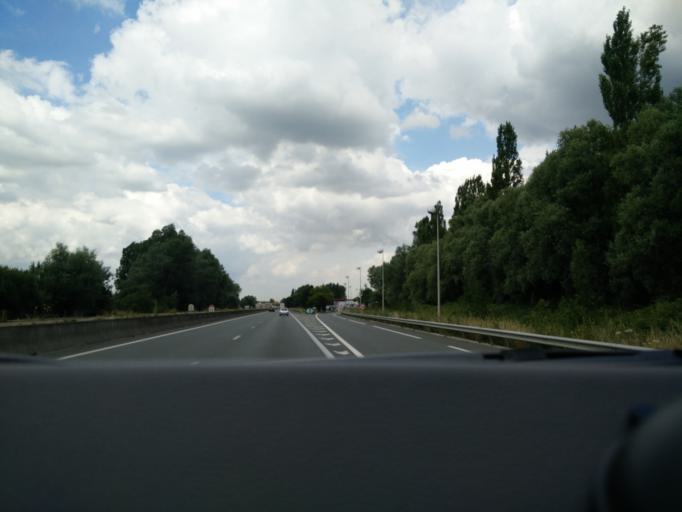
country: FR
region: Nord-Pas-de-Calais
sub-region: Departement du Nord
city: Steenvoorde
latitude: 50.8232
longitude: 2.5873
